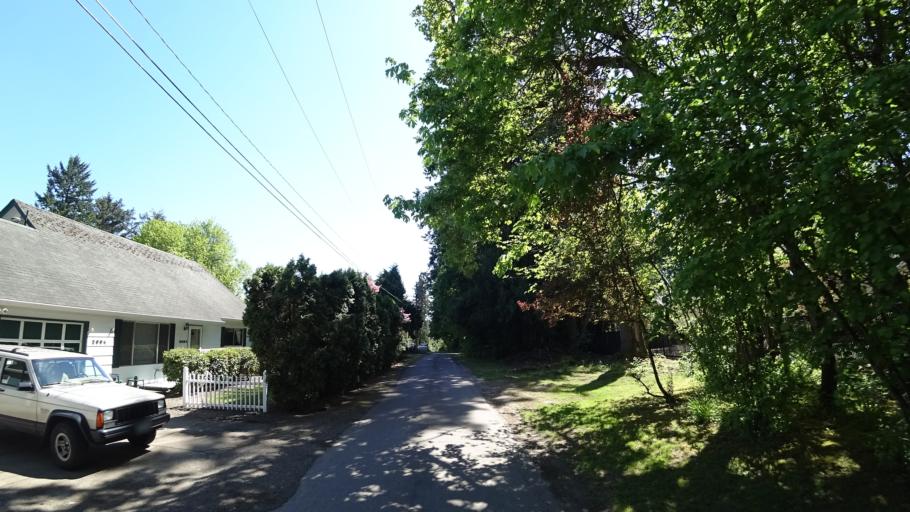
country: US
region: Oregon
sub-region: Washington County
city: Hillsboro
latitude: 45.5040
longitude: -122.9496
